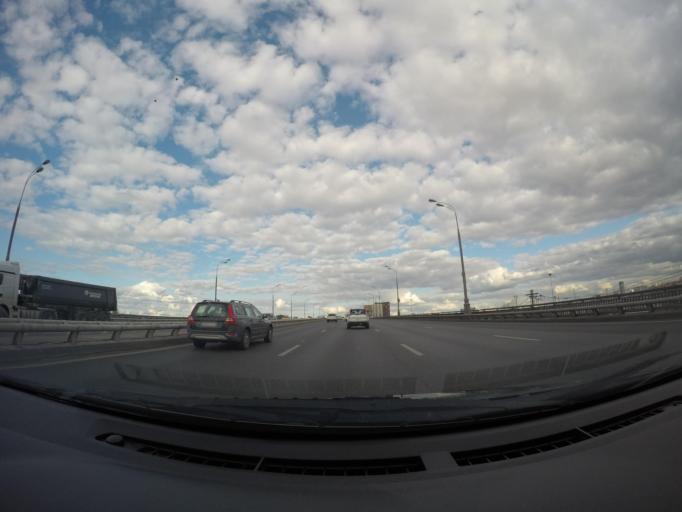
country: RU
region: Moscow
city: Mar'ina Roshcha
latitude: 55.7917
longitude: 37.6418
